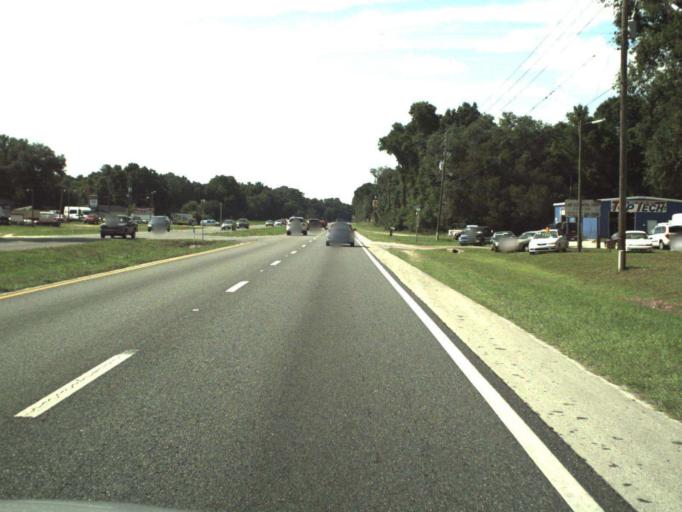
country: US
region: Florida
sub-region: Marion County
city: Belleview
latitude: 29.0911
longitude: -82.0826
